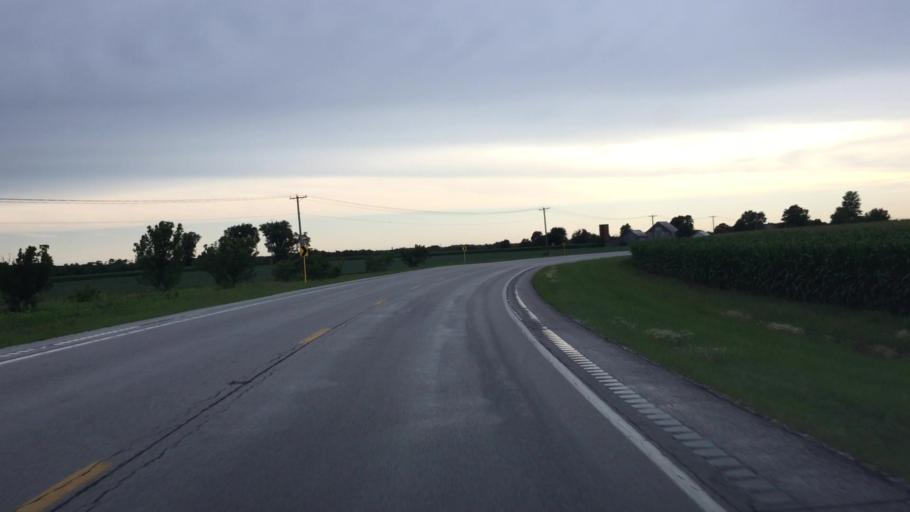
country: US
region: Illinois
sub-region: Hancock County
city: Hamilton
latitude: 40.3636
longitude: -91.3440
